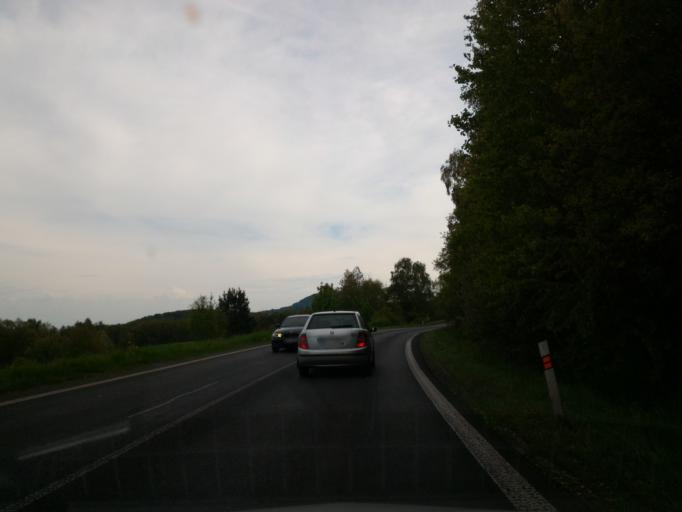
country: CZ
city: Novy Bor
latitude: 50.7402
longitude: 14.5515
